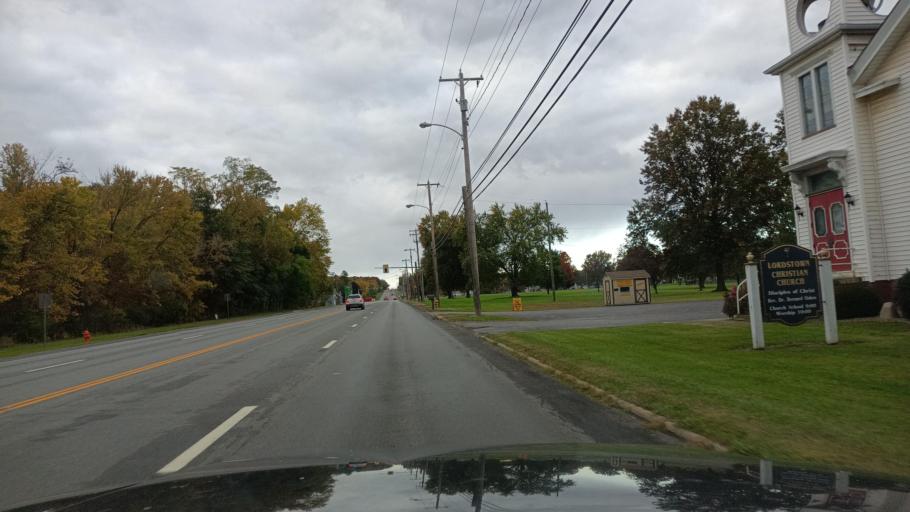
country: US
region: Ohio
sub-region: Trumbull County
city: Lordstown
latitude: 41.1690
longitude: -80.8574
